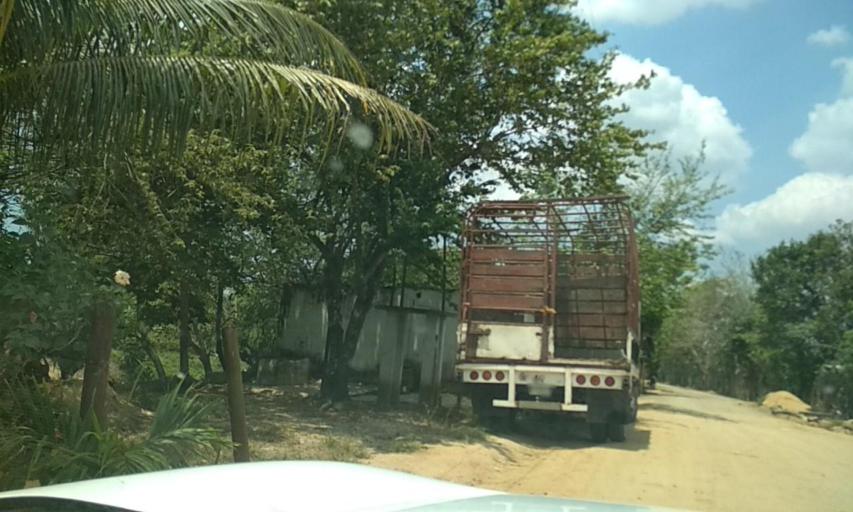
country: MX
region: Veracruz
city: Las Choapas
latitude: 17.9165
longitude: -94.0858
